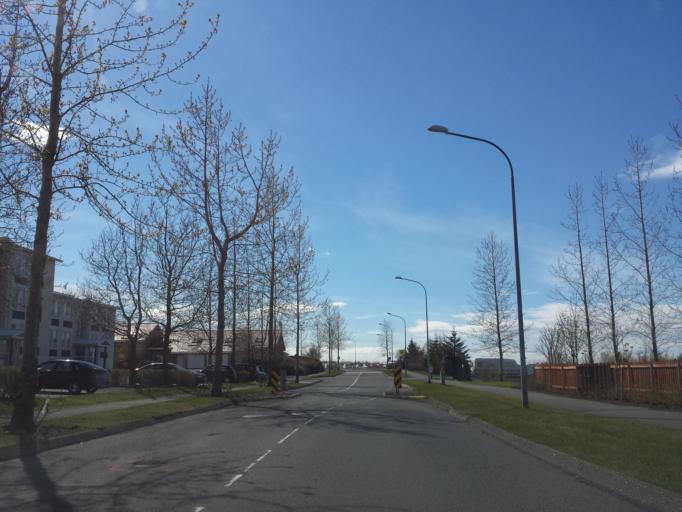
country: IS
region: Capital Region
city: Kopavogur
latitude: 64.1047
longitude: -21.8881
